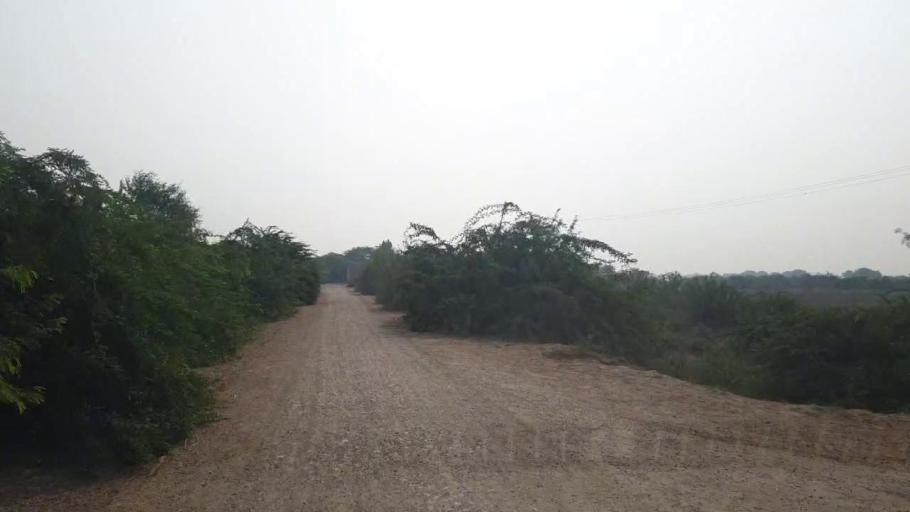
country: PK
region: Sindh
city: Tando Muhammad Khan
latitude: 25.2617
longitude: 68.5118
